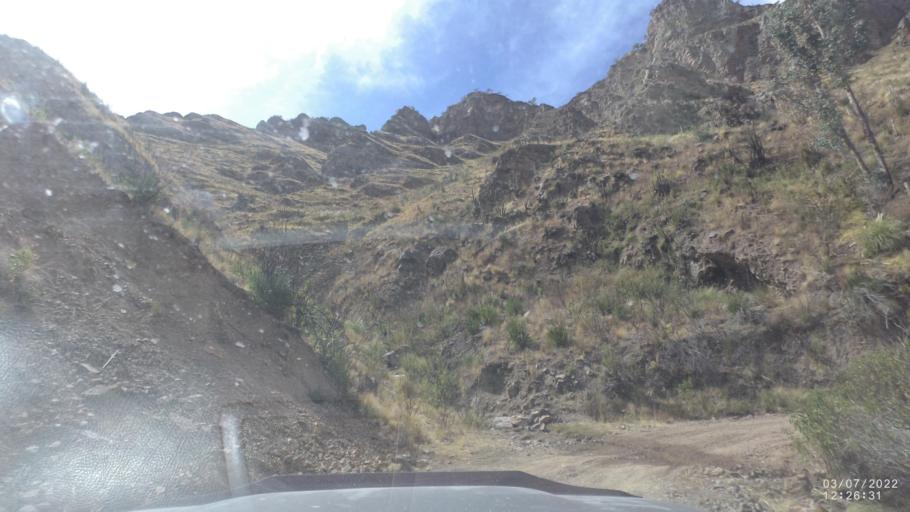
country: BO
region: Cochabamba
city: Irpa Irpa
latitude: -17.8079
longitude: -66.6156
